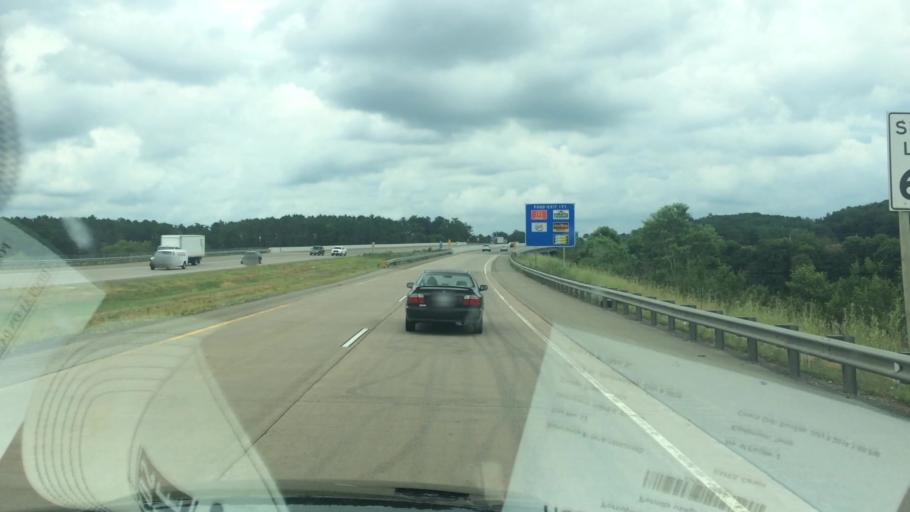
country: US
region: Wisconsin
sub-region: Marathon County
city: Rothschild
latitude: 44.8974
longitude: -89.6226
